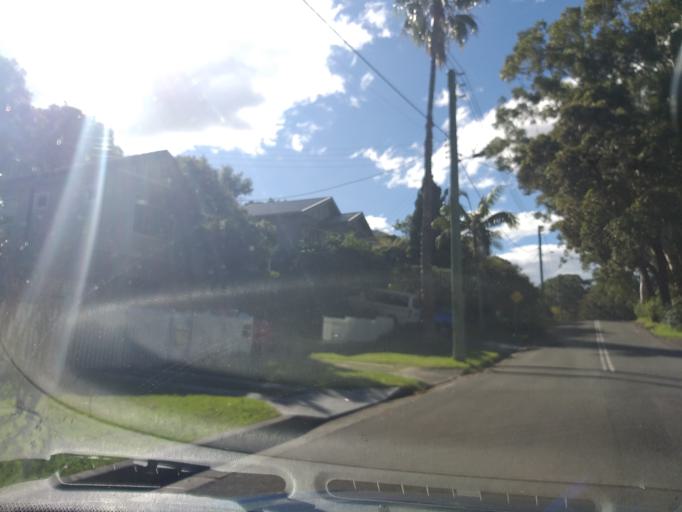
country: AU
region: New South Wales
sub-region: Wollongong
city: Bulli
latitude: -34.3062
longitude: 150.9290
